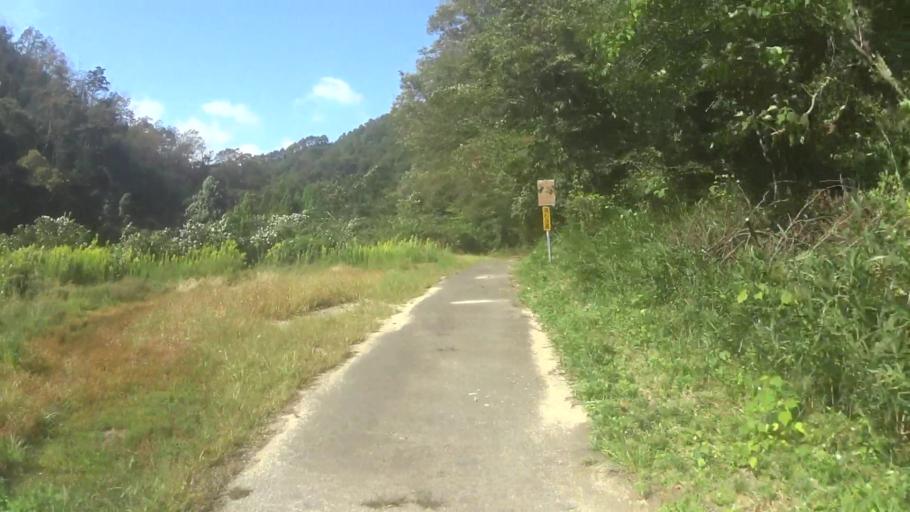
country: JP
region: Kyoto
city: Miyazu
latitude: 35.6984
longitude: 135.1327
